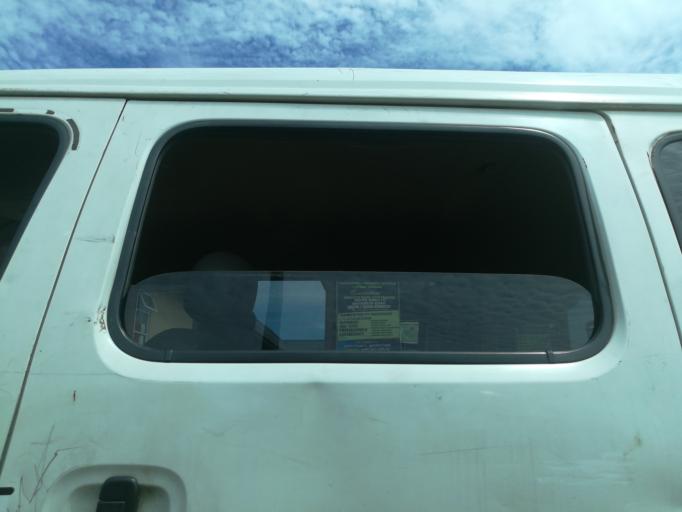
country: NG
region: Lagos
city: Ebute Ikorodu
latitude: 6.5682
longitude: 3.4798
